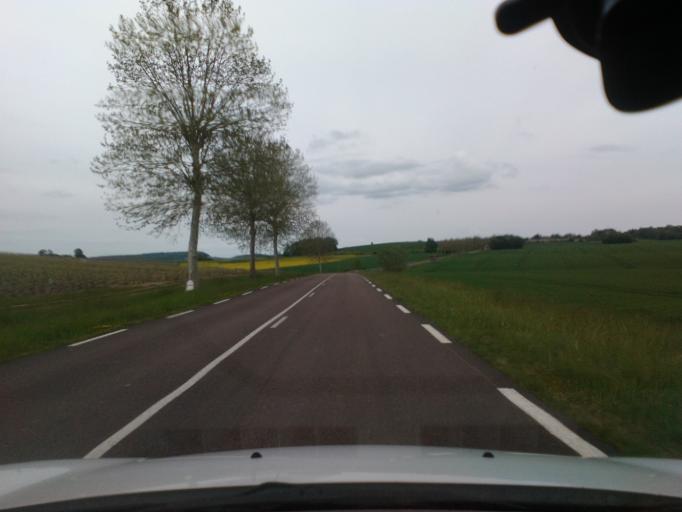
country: FR
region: Champagne-Ardenne
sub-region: Departement de l'Aube
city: Bar-sur-Aube
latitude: 48.2257
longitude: 4.7827
